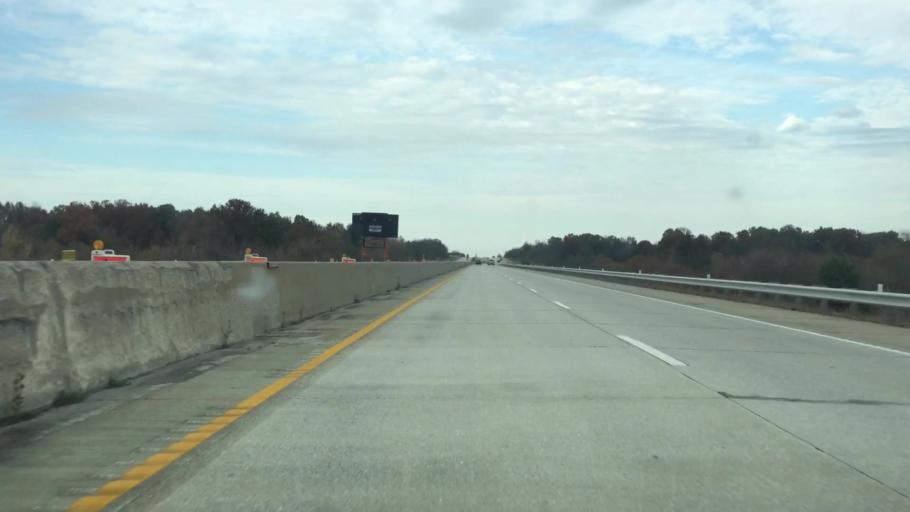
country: US
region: Missouri
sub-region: Henry County
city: Clinton
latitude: 38.2891
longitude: -93.7593
